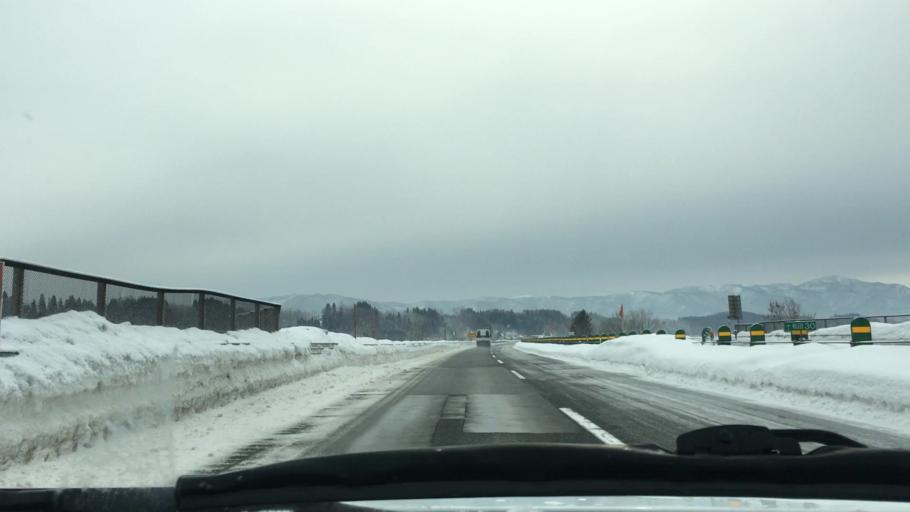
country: JP
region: Akita
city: Hanawa
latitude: 40.2994
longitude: 140.7489
